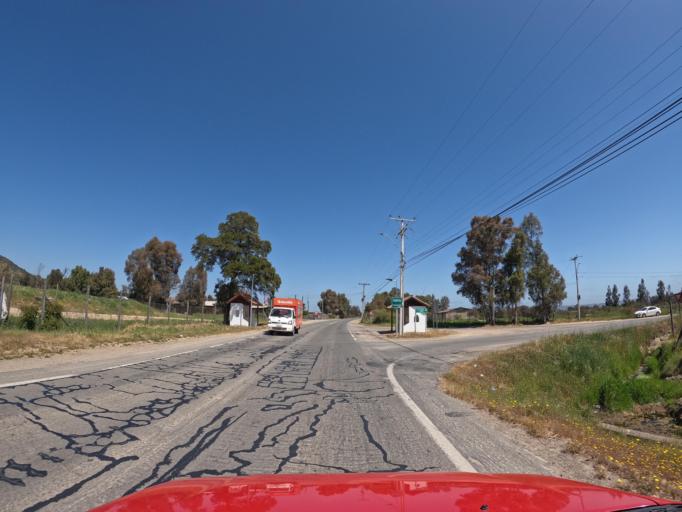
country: CL
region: O'Higgins
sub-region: Provincia de Colchagua
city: Santa Cruz
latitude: -34.7330
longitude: -71.6848
